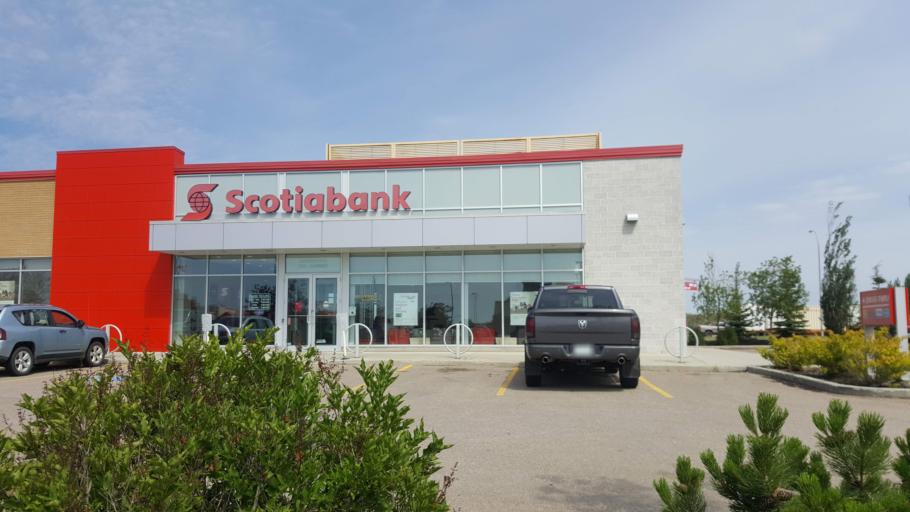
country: CA
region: Saskatchewan
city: Lloydminster
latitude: 53.2783
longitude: -110.0644
